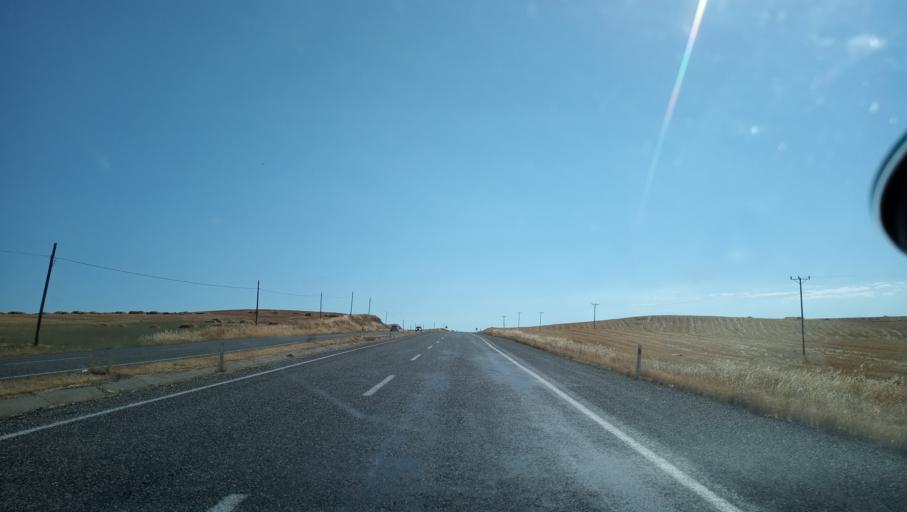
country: TR
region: Diyarbakir
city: Bagdere
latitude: 38.1283
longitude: 40.7548
